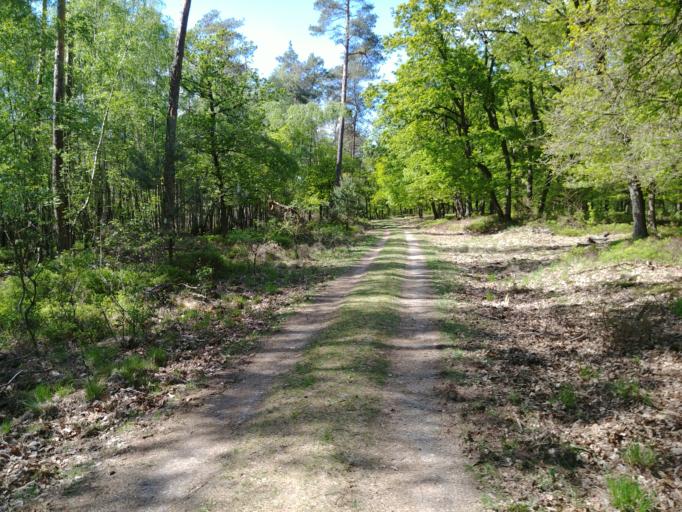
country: NL
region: Gelderland
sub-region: Gemeente Apeldoorn
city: Uddel
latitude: 52.2565
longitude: 5.8601
